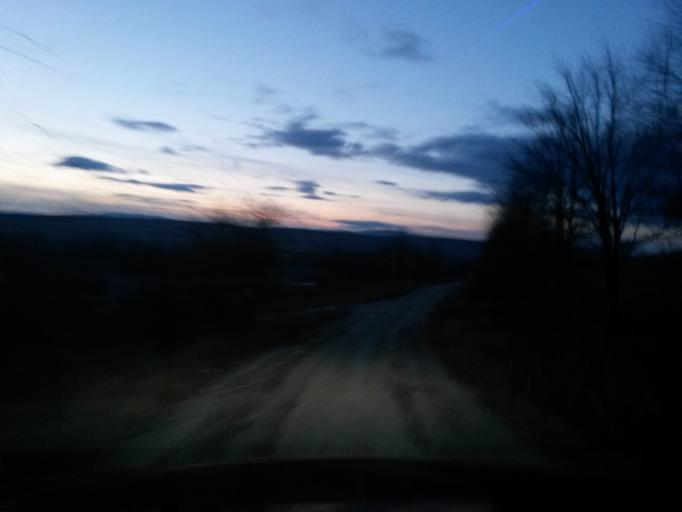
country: SK
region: Kosicky
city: Kosice
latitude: 48.6875
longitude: 21.3518
